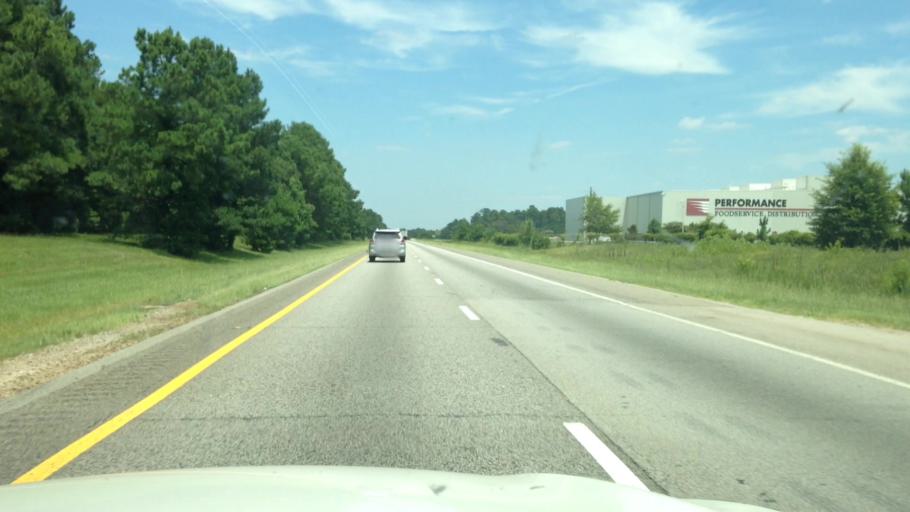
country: US
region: South Carolina
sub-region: Florence County
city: Florence
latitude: 34.2751
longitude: -79.6925
